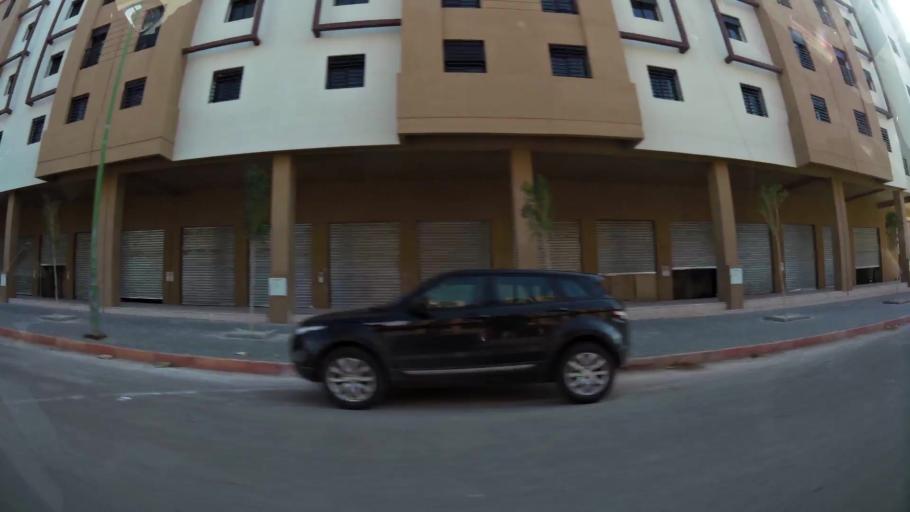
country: MA
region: Marrakech-Tensift-Al Haouz
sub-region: Marrakech
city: Marrakesh
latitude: 31.6861
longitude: -8.0683
